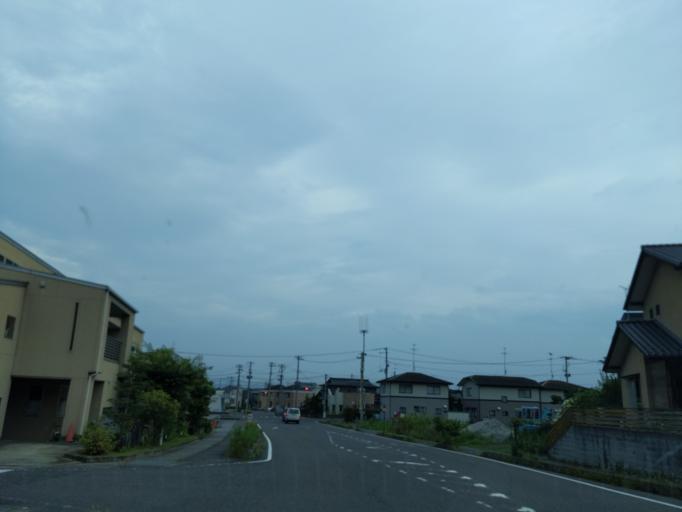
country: JP
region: Fukushima
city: Sukagawa
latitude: 37.3086
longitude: 140.3735
